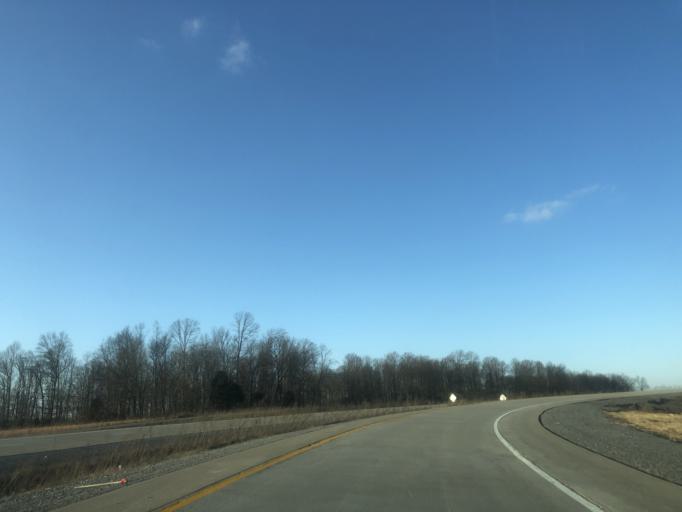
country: US
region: Tennessee
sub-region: Sumner County
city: Portland
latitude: 36.6299
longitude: -86.5774
